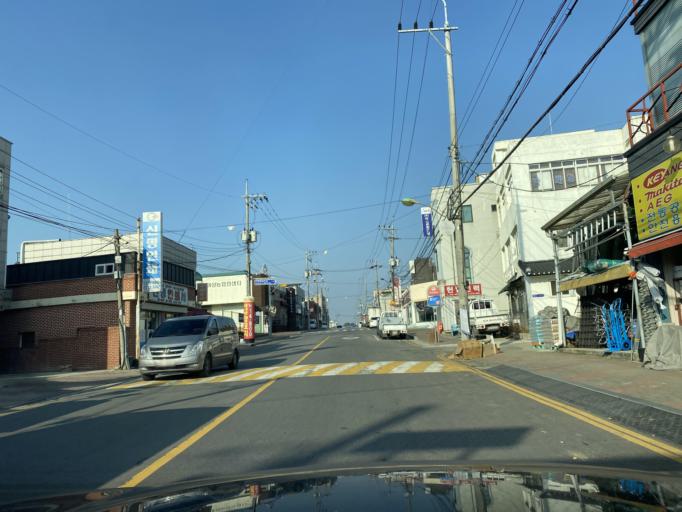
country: KR
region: Chungcheongnam-do
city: Yesan
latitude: 36.6828
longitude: 126.8292
